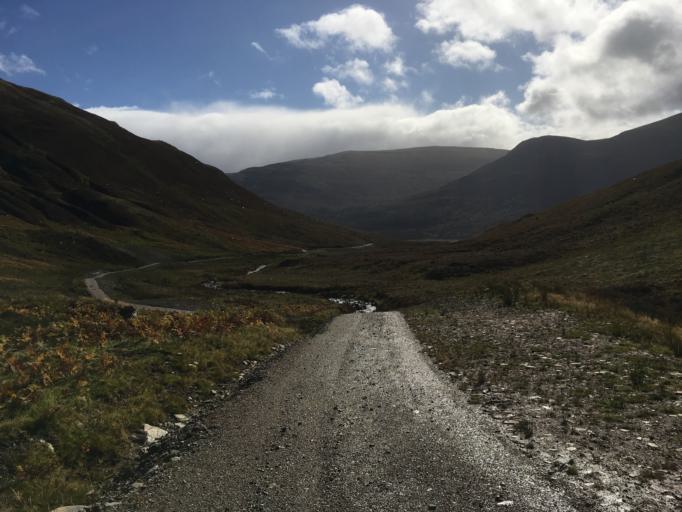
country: GB
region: Scotland
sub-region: Highland
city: Spean Bridge
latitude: 57.3517
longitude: -4.9866
